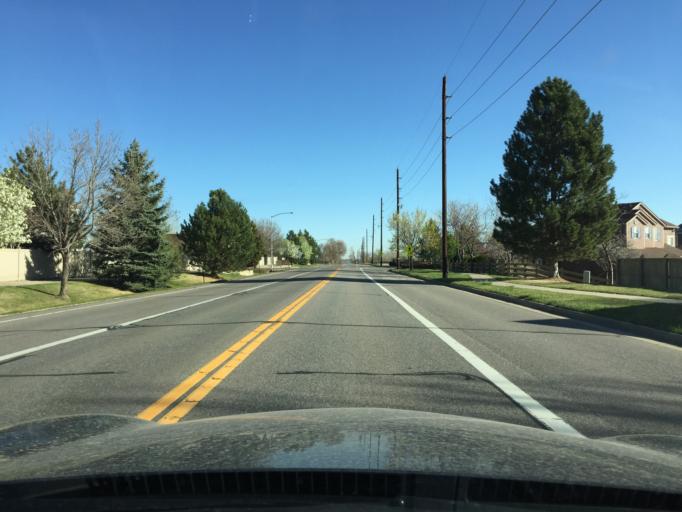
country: US
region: Colorado
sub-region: Boulder County
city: Erie
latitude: 40.0413
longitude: -105.0745
